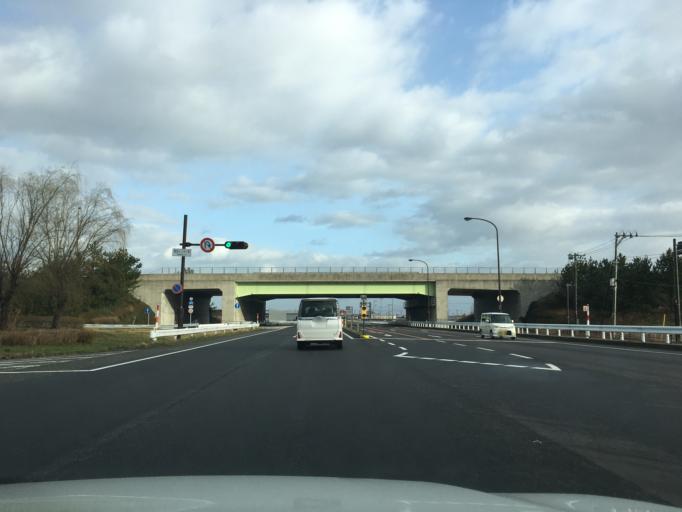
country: JP
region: Yamagata
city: Sakata
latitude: 38.8685
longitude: 139.8421
